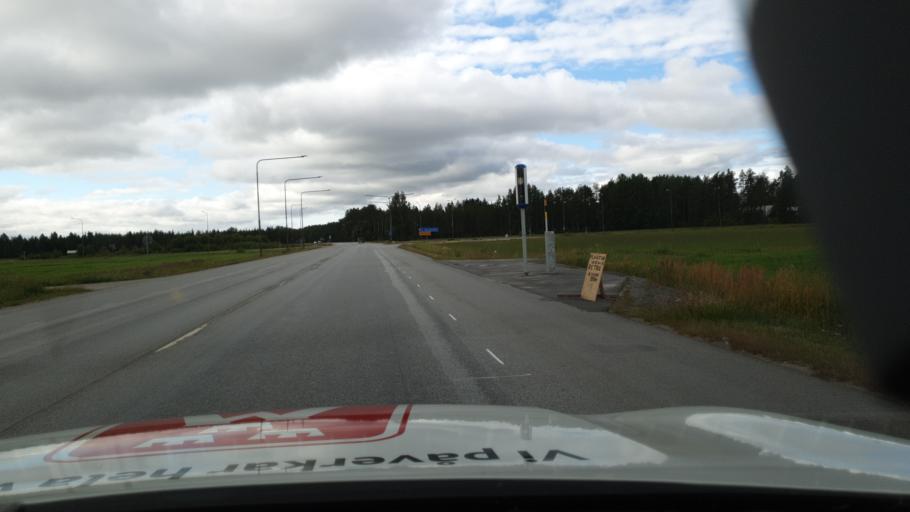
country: SE
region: Vaesterbotten
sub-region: Umea Kommun
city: Roback
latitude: 63.7782
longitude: 20.2035
